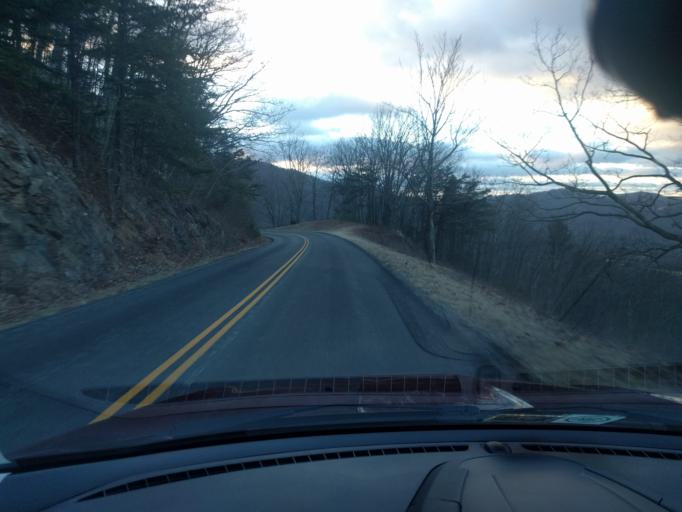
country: US
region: Virginia
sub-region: Botetourt County
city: Buchanan
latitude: 37.4769
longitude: -79.6516
